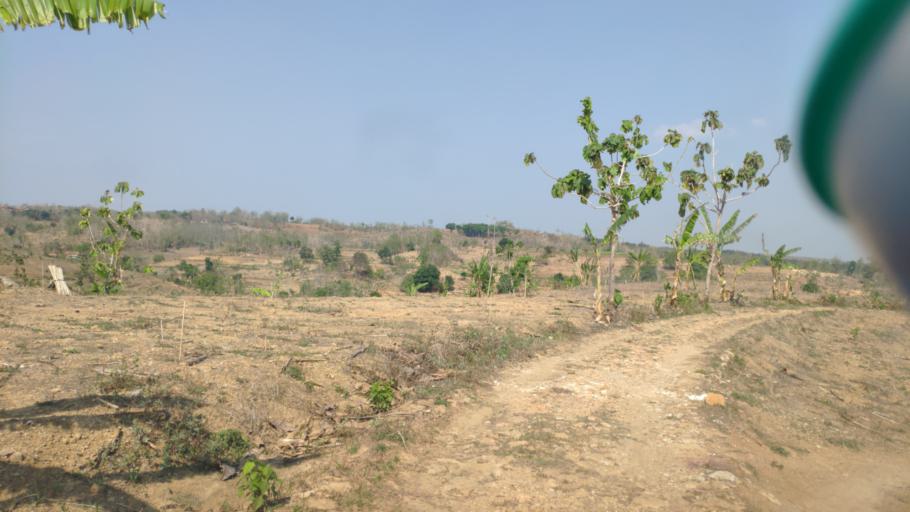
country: ID
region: Central Java
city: Ngapus
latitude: -6.9280
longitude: 111.2130
